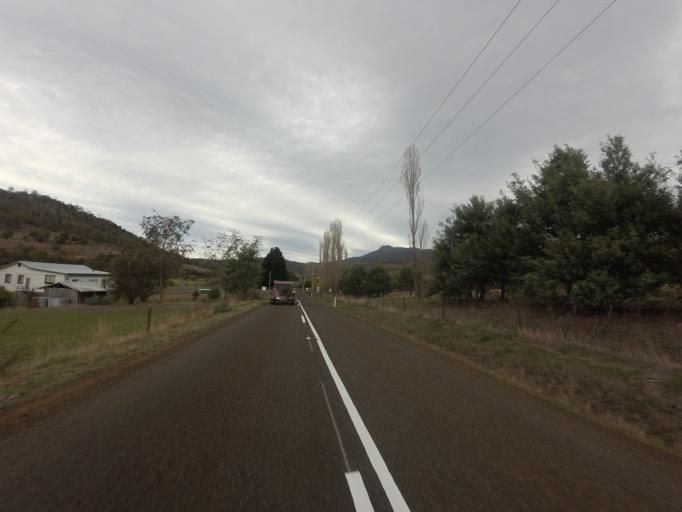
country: AU
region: Tasmania
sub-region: Brighton
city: Bridgewater
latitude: -42.6559
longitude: 147.1258
